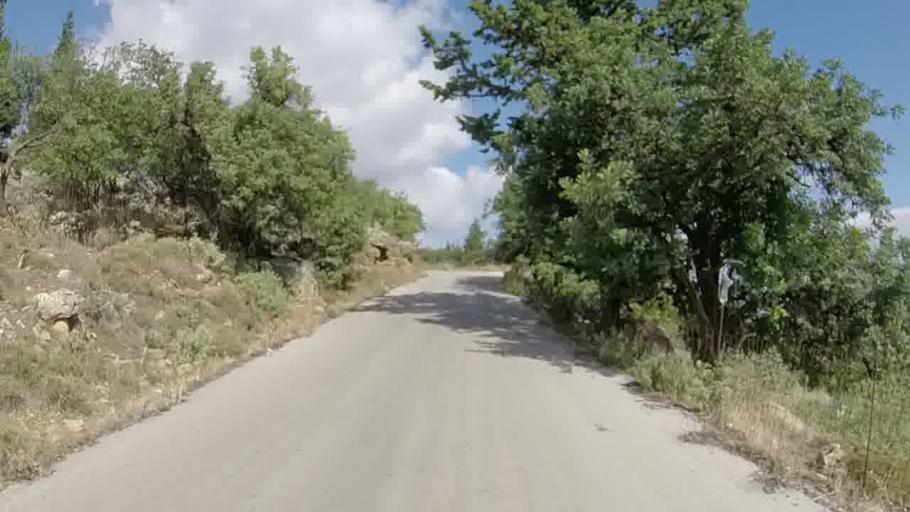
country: GR
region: Crete
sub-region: Nomos Chanias
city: Kalivai
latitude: 35.3879
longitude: 24.1325
